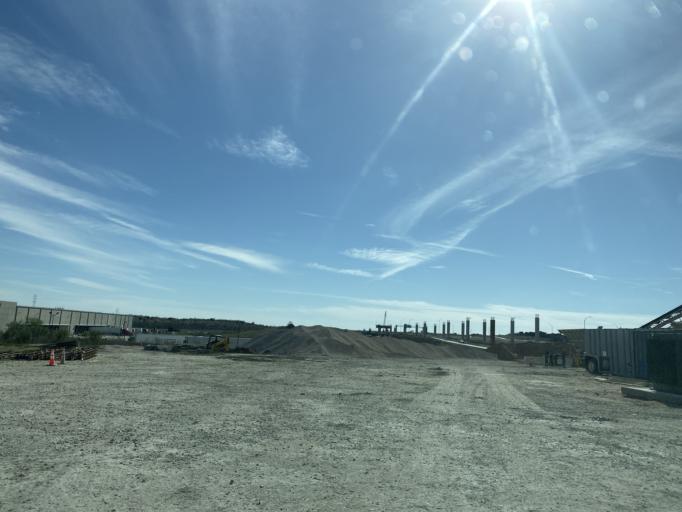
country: US
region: Texas
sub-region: Travis County
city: Manor
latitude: 30.3403
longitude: -97.5891
